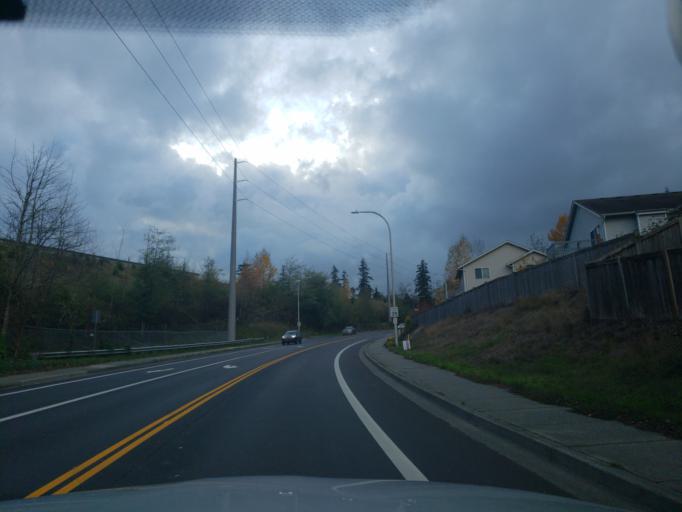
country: US
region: Washington
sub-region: Snohomish County
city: Everett
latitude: 47.9441
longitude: -122.2439
